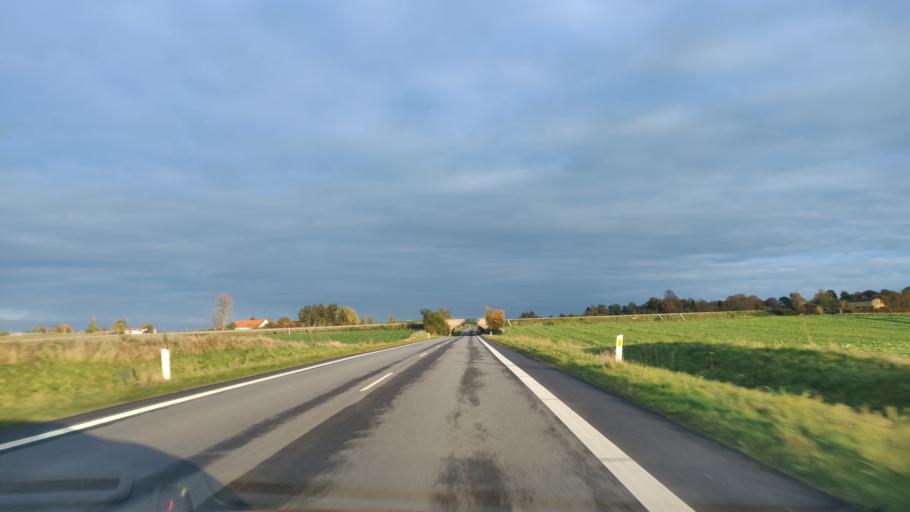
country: DK
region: Zealand
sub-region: Holbaek Kommune
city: Vipperod
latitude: 55.6837
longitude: 11.7203
